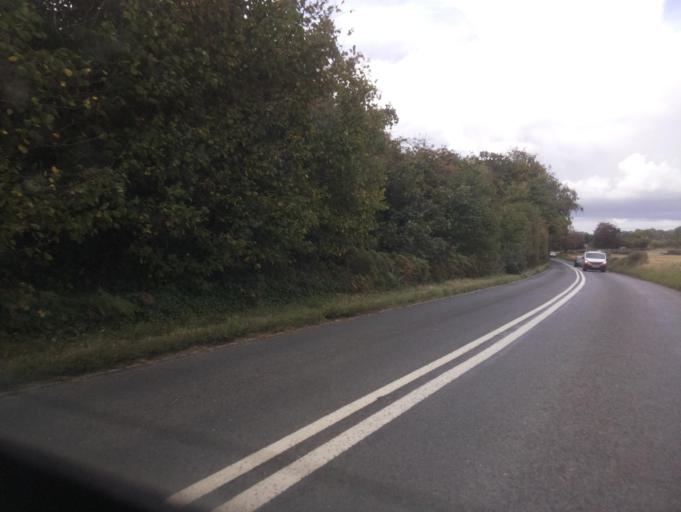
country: GB
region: England
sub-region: Staffordshire
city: Gnosall
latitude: 52.8165
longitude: -2.3118
